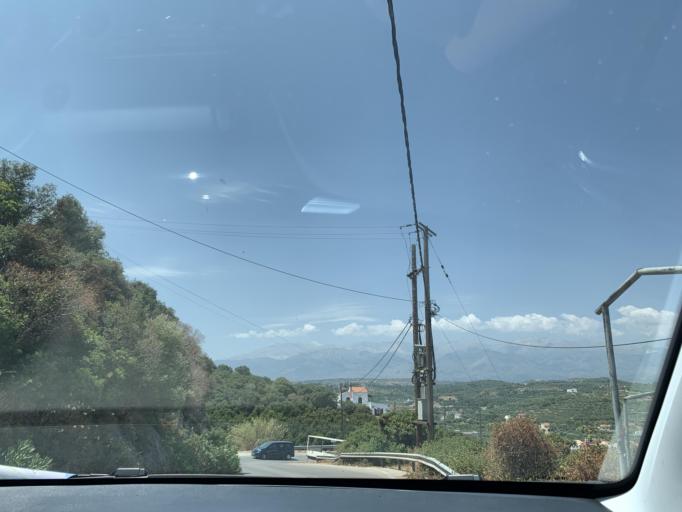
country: GR
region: Crete
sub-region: Nomos Chanias
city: Kalivai
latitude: 35.4487
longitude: 24.2064
